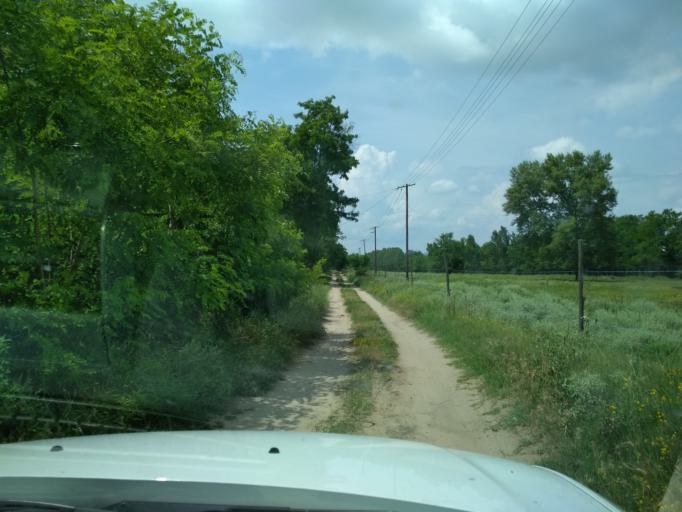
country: HU
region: Pest
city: Tapioszentmarton
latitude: 47.3713
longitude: 19.7786
